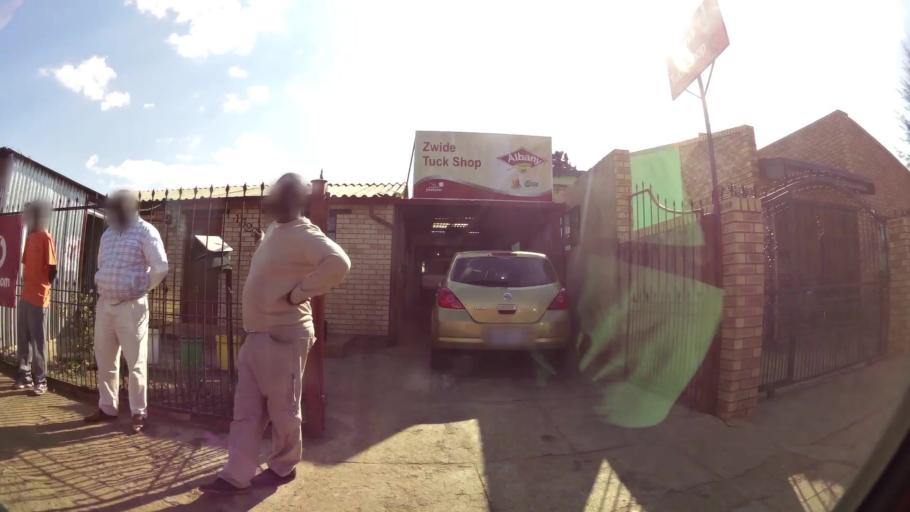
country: ZA
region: Gauteng
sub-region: City of Johannesburg Metropolitan Municipality
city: Soweto
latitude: -26.2298
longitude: 27.8807
